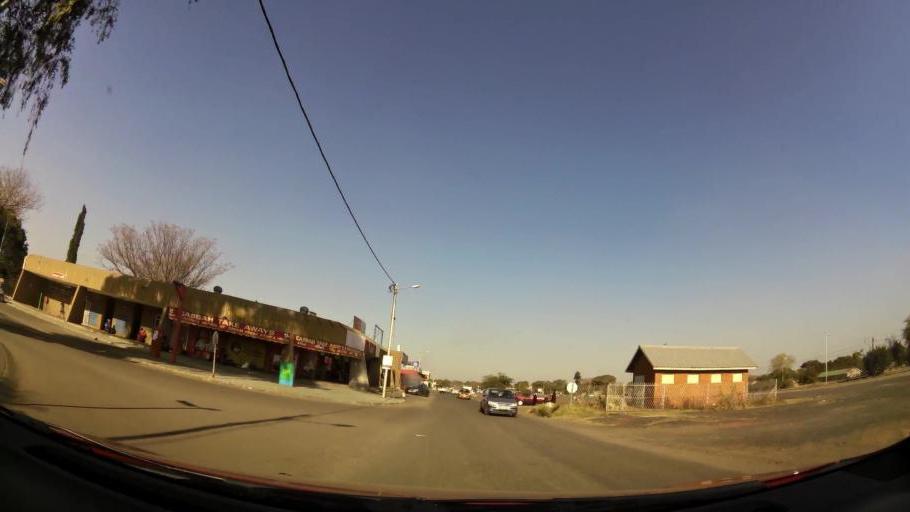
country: ZA
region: North-West
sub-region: Bojanala Platinum District Municipality
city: Rustenburg
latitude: -25.6480
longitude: 27.2368
